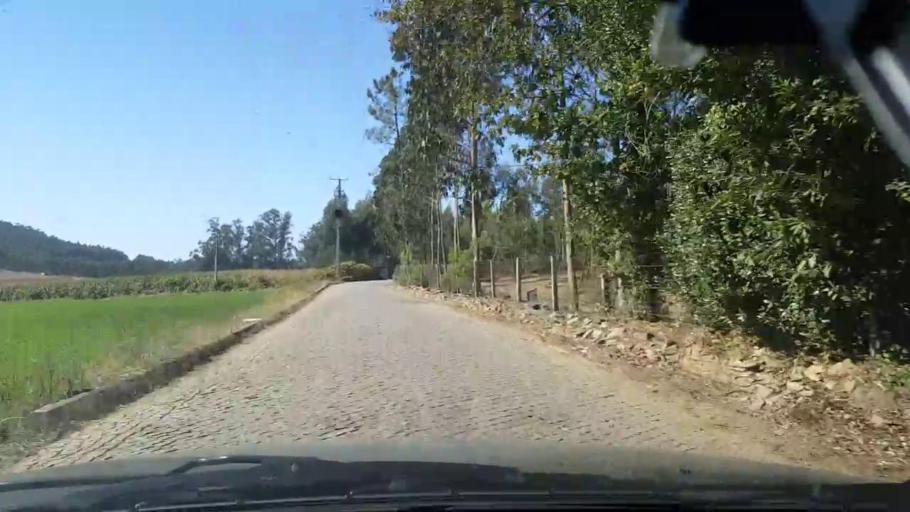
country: PT
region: Braga
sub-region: Vila Nova de Famalicao
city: Ribeirao
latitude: 41.3907
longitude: -8.6358
